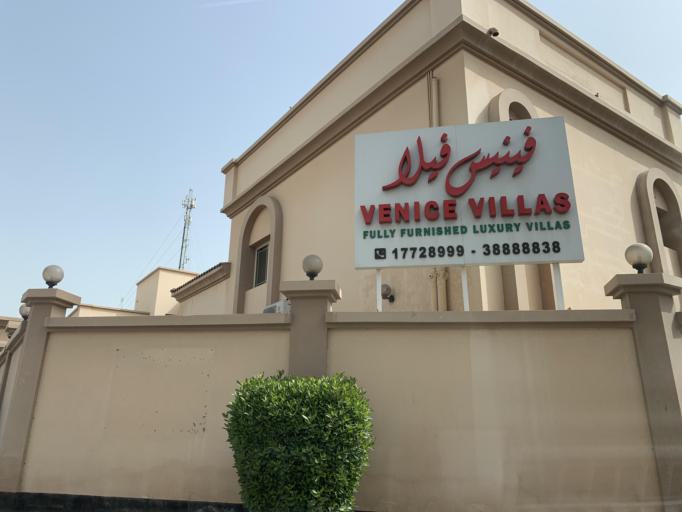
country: BH
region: Manama
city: Manama
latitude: 26.2120
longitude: 50.6135
